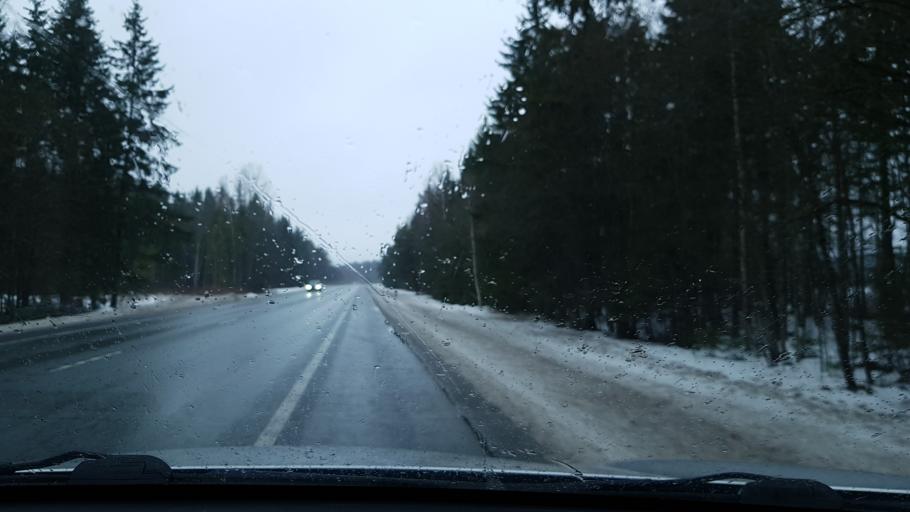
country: EE
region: Raplamaa
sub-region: Kohila vald
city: Kohila
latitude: 59.1570
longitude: 24.7766
